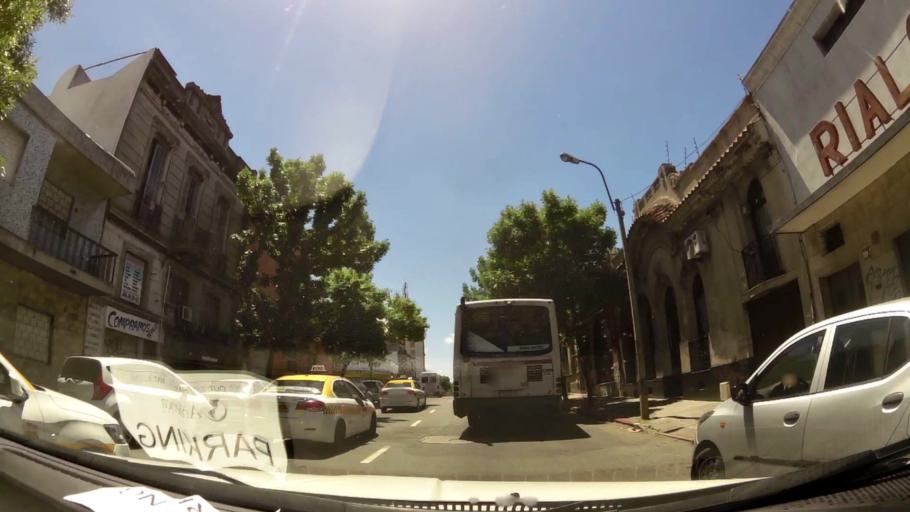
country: UY
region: Montevideo
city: Montevideo
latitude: -34.8961
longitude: -56.1823
